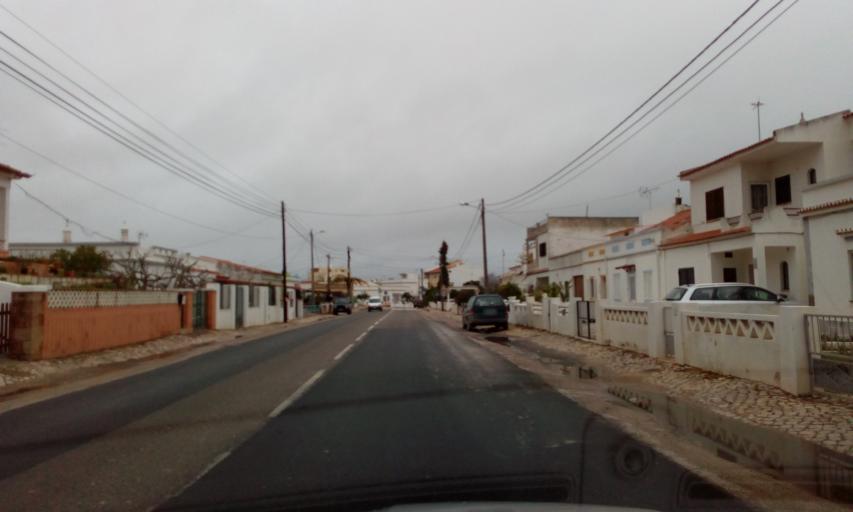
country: PT
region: Faro
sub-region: Albufeira
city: Guia
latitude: 37.1615
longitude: -8.2996
